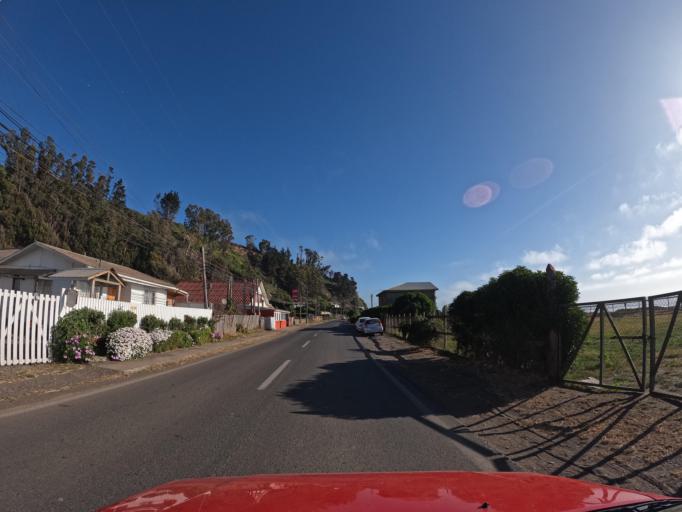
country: CL
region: Maule
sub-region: Provincia de Talca
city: Constitucion
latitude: -34.9048
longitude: -72.1802
